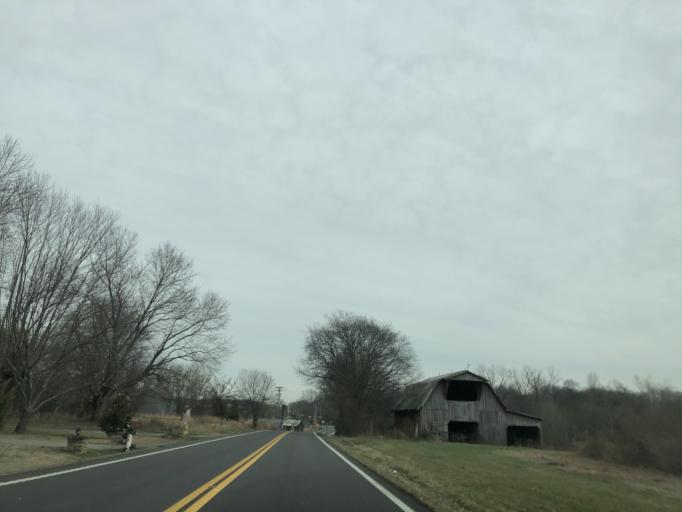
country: US
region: Tennessee
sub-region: Sumner County
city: White House
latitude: 36.4750
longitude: -86.7148
